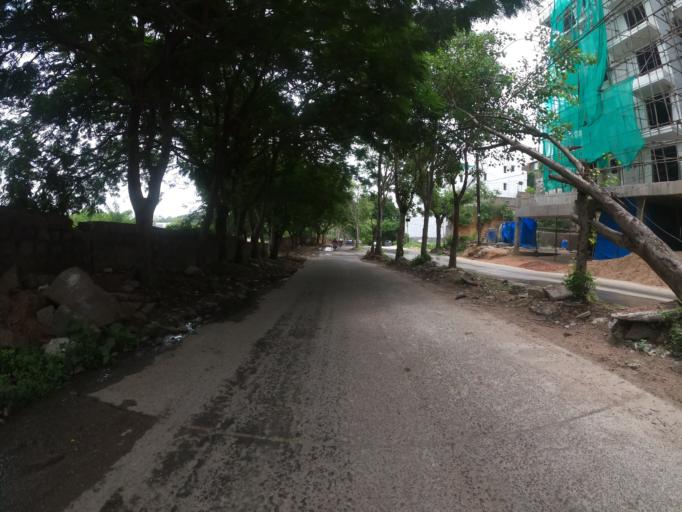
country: IN
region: Telangana
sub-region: Rangareddi
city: Kukatpalli
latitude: 17.4231
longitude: 78.3988
